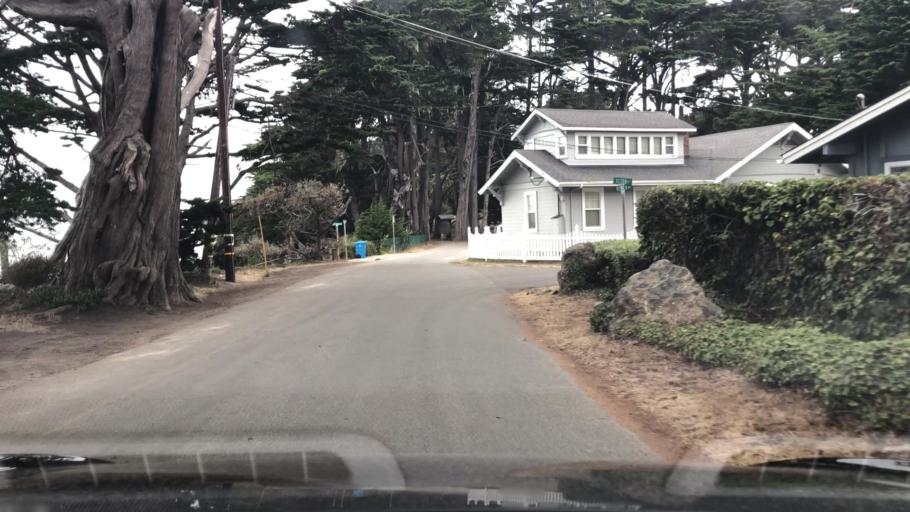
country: US
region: California
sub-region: San Mateo County
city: Moss Beach
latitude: 37.5192
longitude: -122.5129
